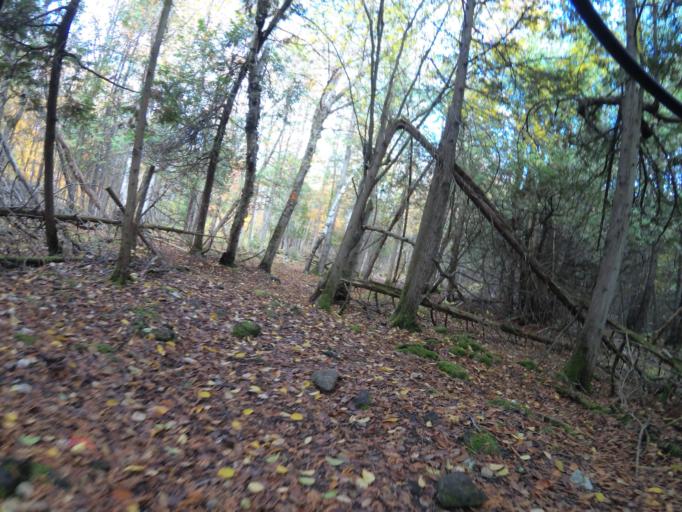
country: CA
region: Ontario
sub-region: Lanark County
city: Smiths Falls
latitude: 45.0312
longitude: -75.8034
